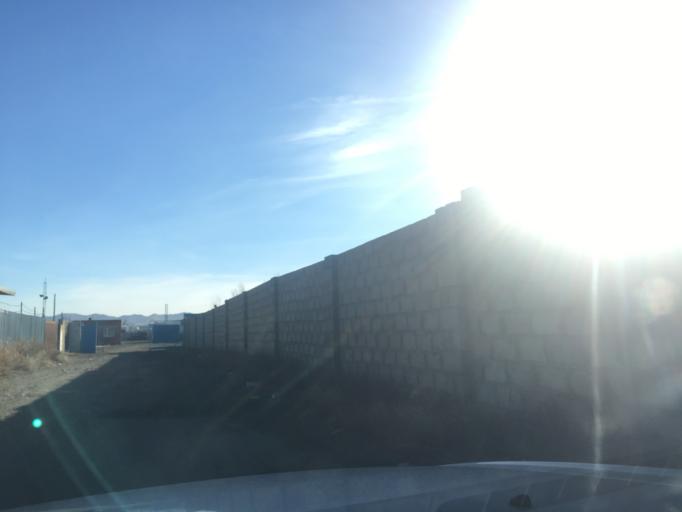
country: MN
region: Ulaanbaatar
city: Ulaanbaatar
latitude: 47.9014
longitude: 106.7754
